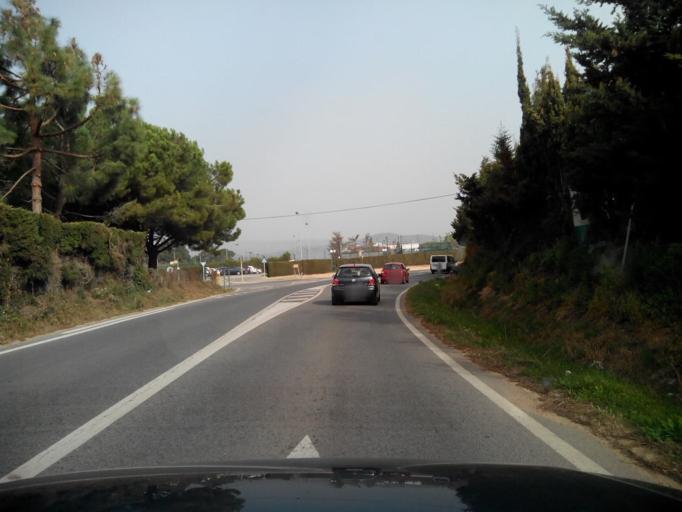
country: ES
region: Catalonia
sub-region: Provincia de Tarragona
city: Reus
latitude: 41.1359
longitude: 1.0960
